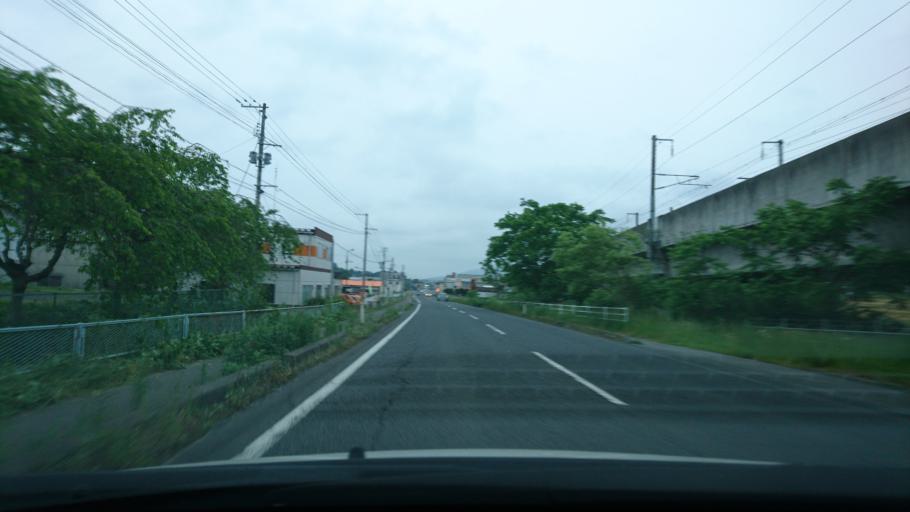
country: JP
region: Iwate
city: Ichinoseki
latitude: 38.9055
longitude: 141.1306
